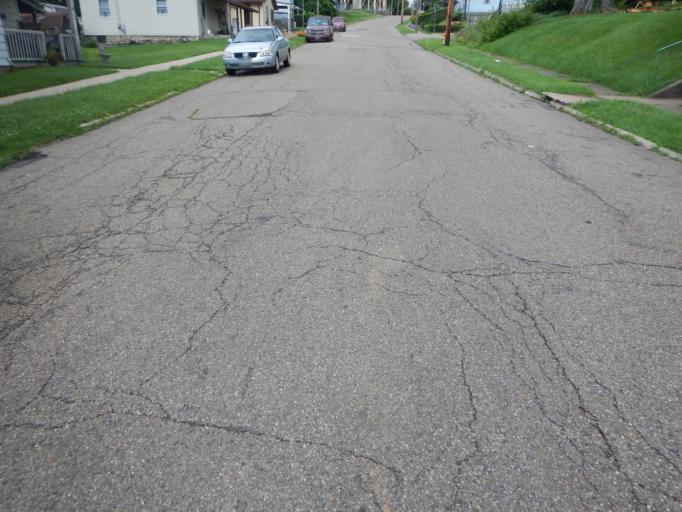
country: US
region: Ohio
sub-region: Muskingum County
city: Zanesville
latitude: 39.9325
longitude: -82.0152
